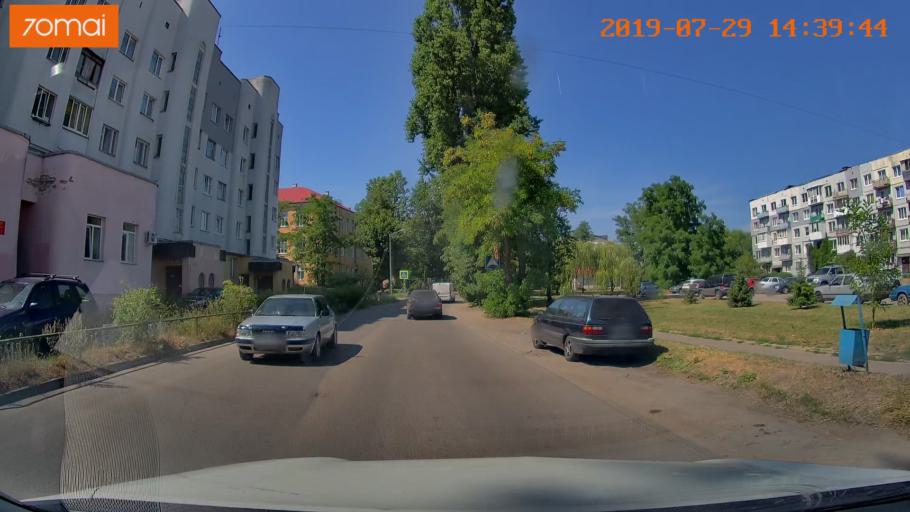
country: RU
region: Kaliningrad
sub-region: Gorod Kaliningrad
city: Baltiysk
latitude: 54.6527
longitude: 19.9036
